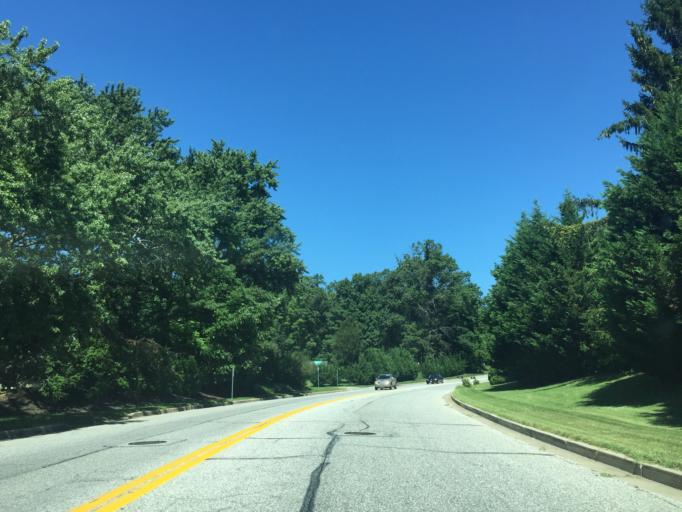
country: US
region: Maryland
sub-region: Baltimore County
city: Timonium
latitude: 39.4300
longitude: -76.6029
